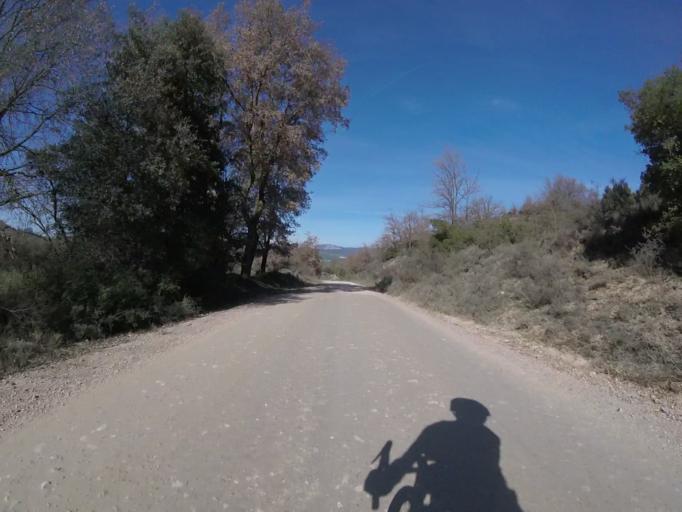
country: ES
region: Navarre
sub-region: Provincia de Navarra
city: Villatuerta
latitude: 42.6481
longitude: -1.9675
